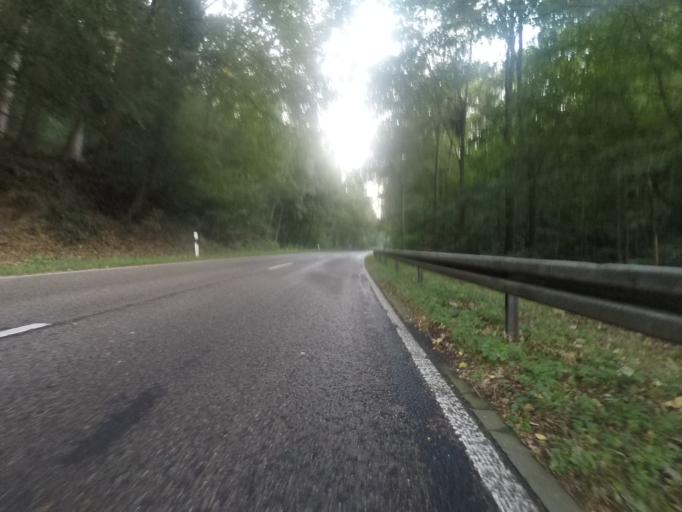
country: DE
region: Baden-Wuerttemberg
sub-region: Karlsruhe Region
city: Ettlingen
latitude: 48.9165
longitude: 8.3962
